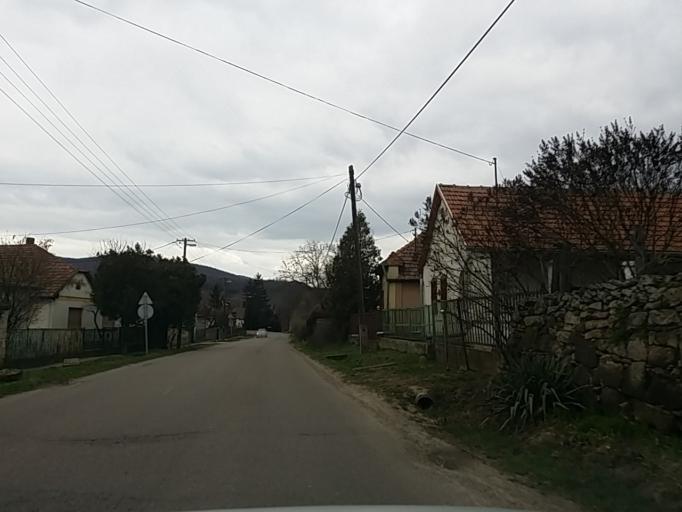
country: HU
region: Heves
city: Verpelet
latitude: 47.8776
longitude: 20.2012
